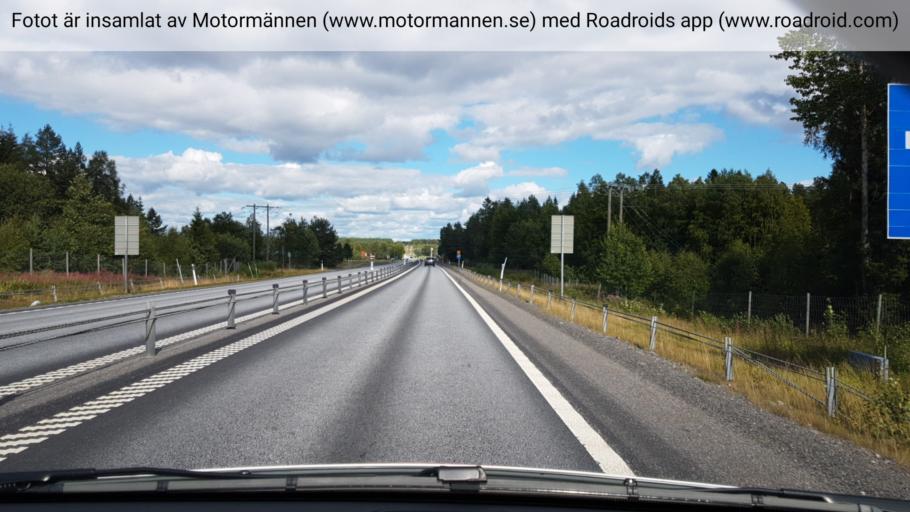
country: SE
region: Vaesterbotten
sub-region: Umea Kommun
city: Hoernefors
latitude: 63.6766
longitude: 19.9907
